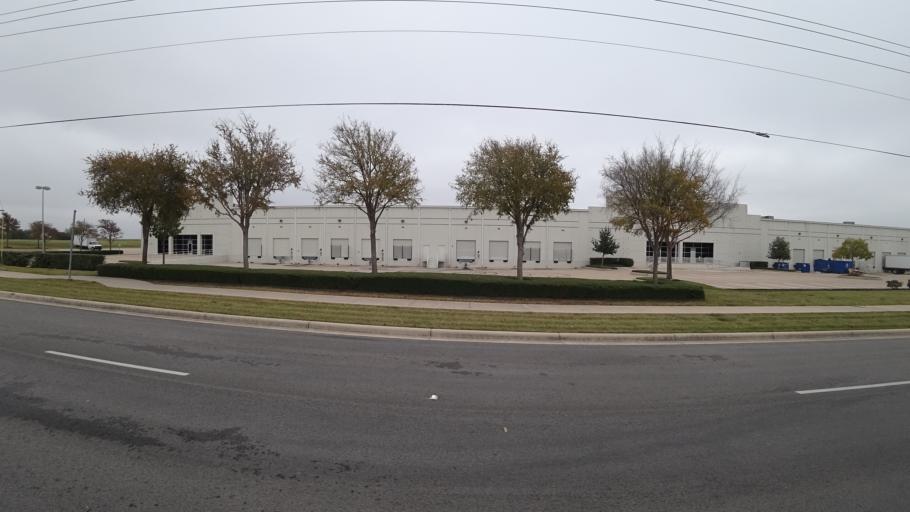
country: US
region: Texas
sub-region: Travis County
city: Manor
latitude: 30.3752
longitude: -97.6102
